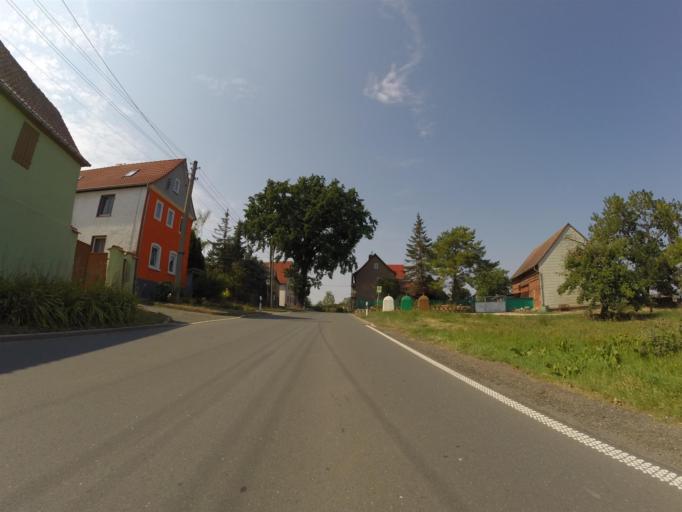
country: DE
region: Thuringia
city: Schongleina
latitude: 50.9278
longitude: 11.7225
